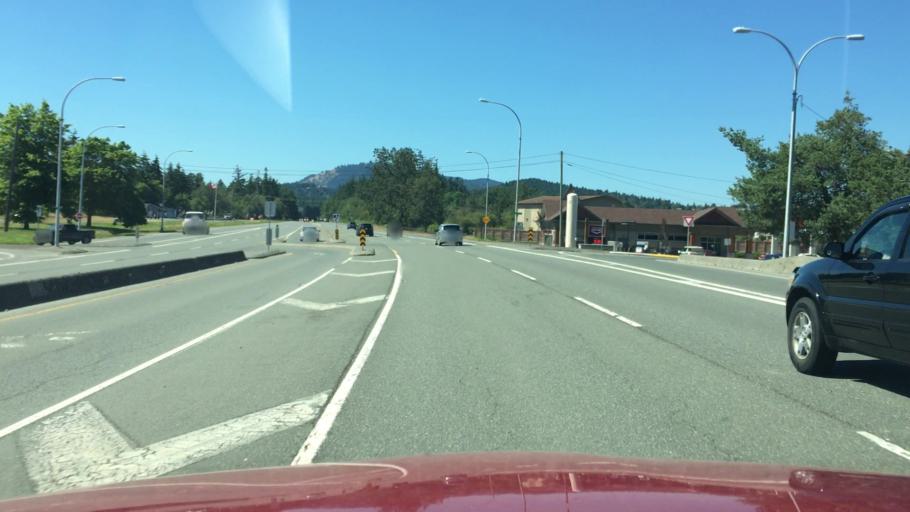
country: CA
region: British Columbia
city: North Saanich
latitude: 48.6627
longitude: -123.4170
